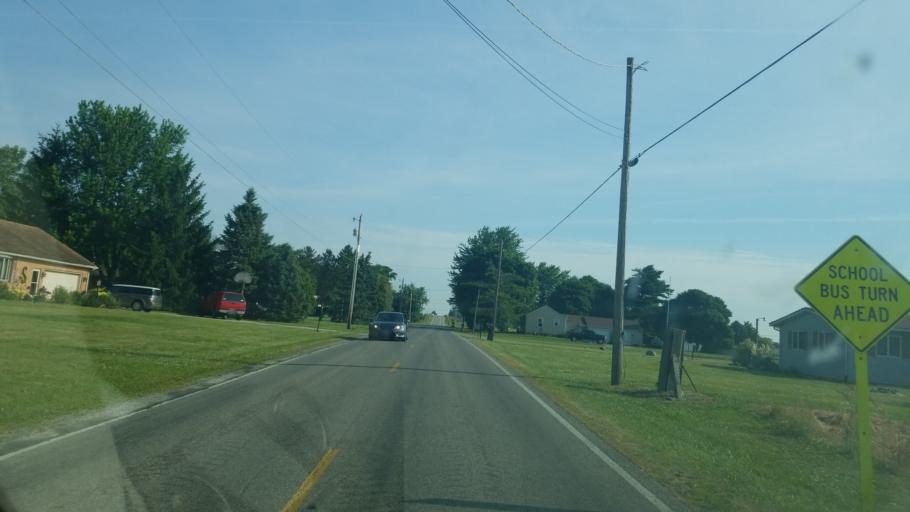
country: US
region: Ohio
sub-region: Hancock County
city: Findlay
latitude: 40.9885
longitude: -83.6985
